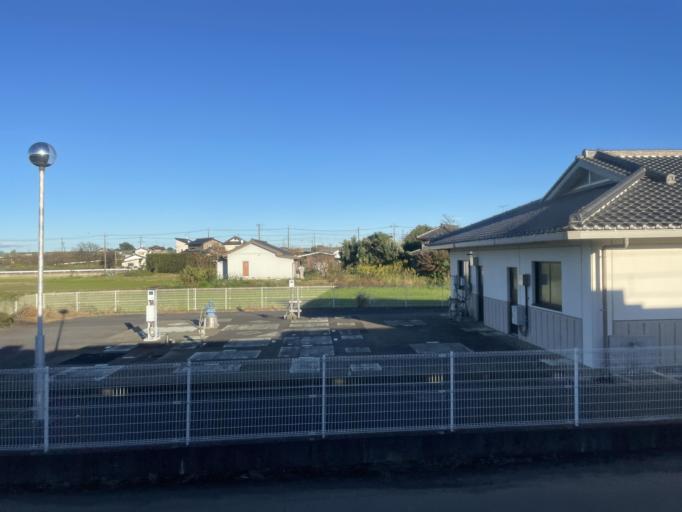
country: JP
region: Saitama
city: Satte
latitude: 36.1031
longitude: 139.7209
